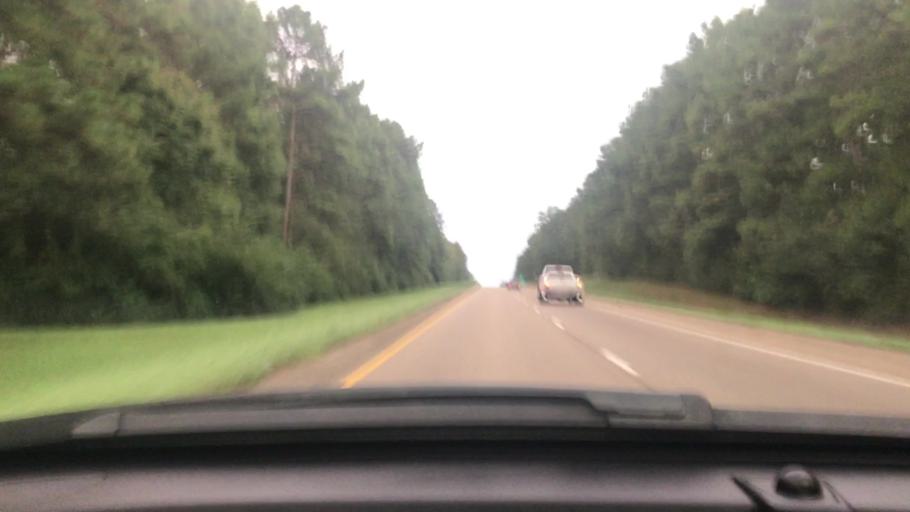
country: US
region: Louisiana
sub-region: Tangipahoa Parish
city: Roseland
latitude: 30.8465
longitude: -90.5334
